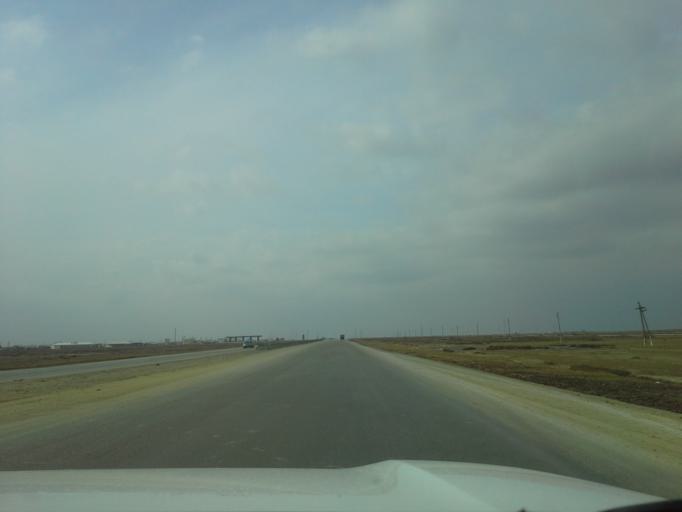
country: IR
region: Razavi Khorasan
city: Kalat-e Naderi
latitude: 37.2043
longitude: 60.0318
